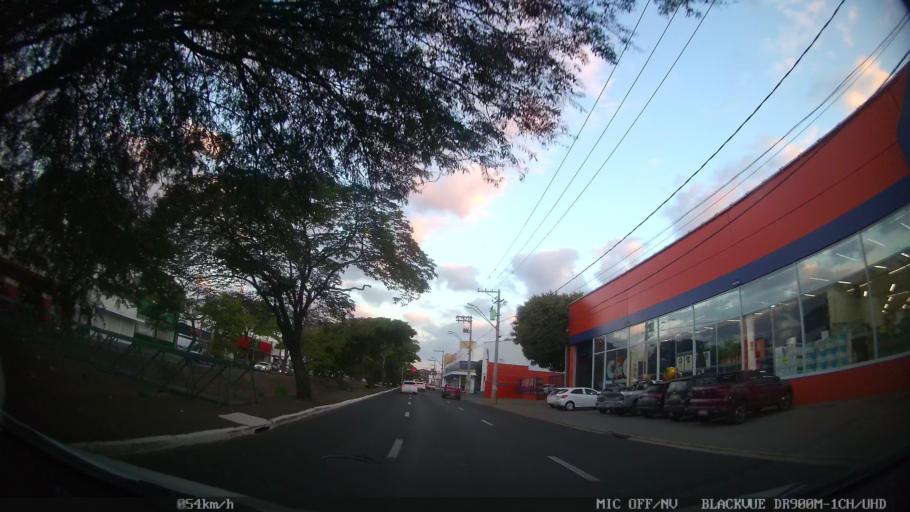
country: BR
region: Sao Paulo
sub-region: Ribeirao Preto
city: Ribeirao Preto
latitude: -21.1850
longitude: -47.7995
